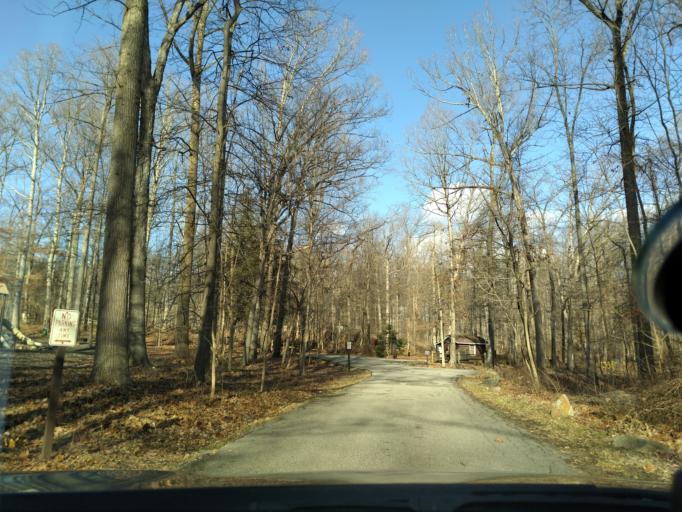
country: US
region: Maryland
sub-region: Howard County
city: Ilchester
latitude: 39.2450
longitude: -76.7450
